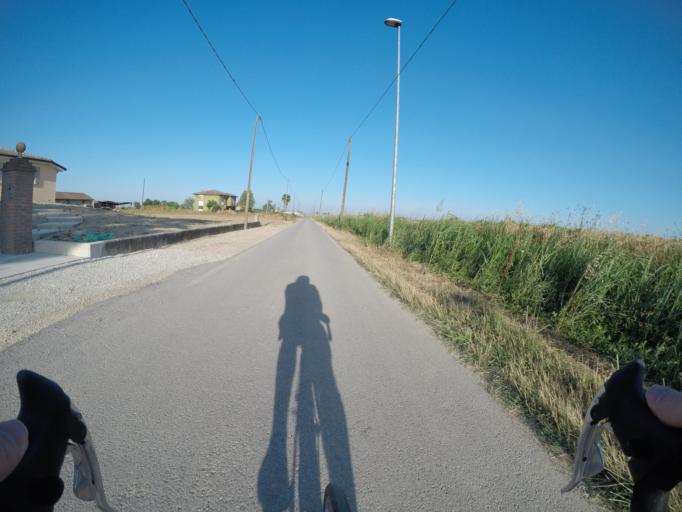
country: IT
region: Veneto
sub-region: Provincia di Rovigo
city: Fratta Polesine
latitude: 45.0272
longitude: 11.6579
